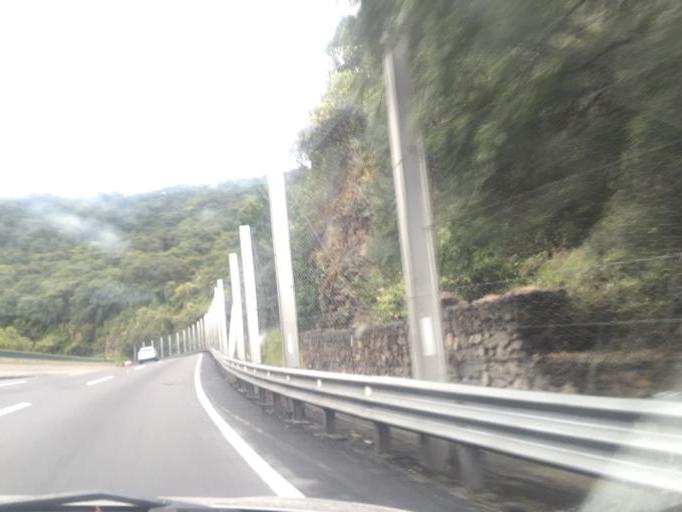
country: MX
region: Mexico City
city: Xochimilco
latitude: 19.2240
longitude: -99.1394
